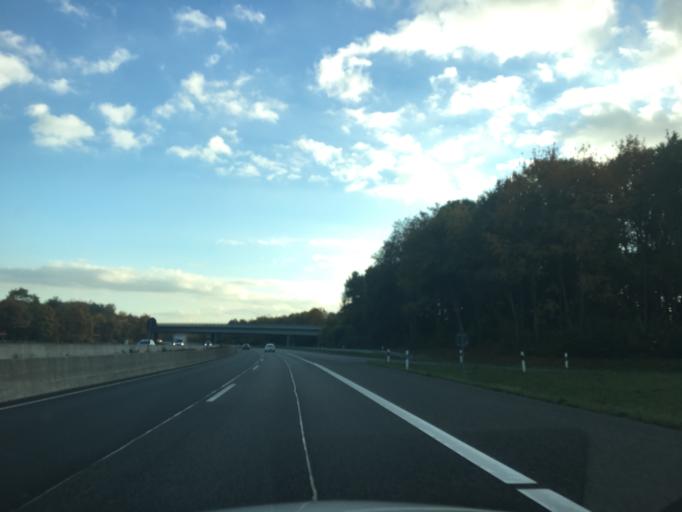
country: DE
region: Hesse
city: Langen
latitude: 49.9960
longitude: 8.6885
